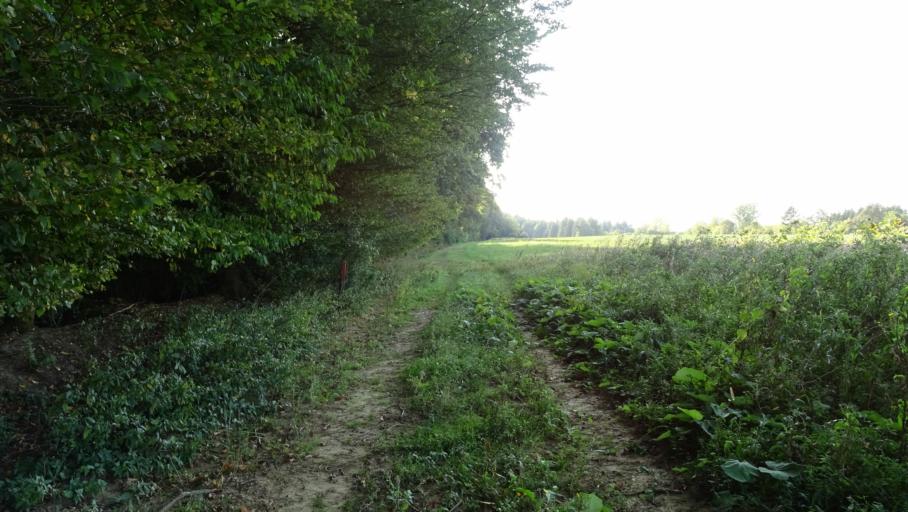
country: DE
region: Baden-Wuerttemberg
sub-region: Karlsruhe Region
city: Fahrenbach
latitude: 49.4053
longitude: 9.1649
